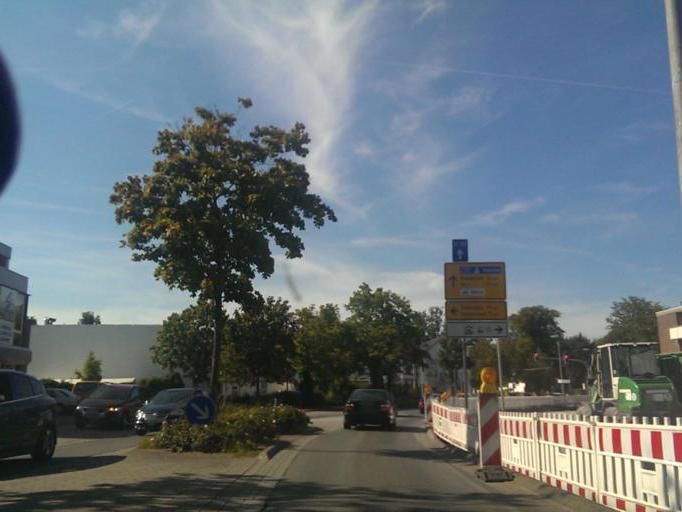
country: DE
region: North Rhine-Westphalia
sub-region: Regierungsbezirk Detmold
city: Hovelhof
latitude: 51.8195
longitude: 8.6590
